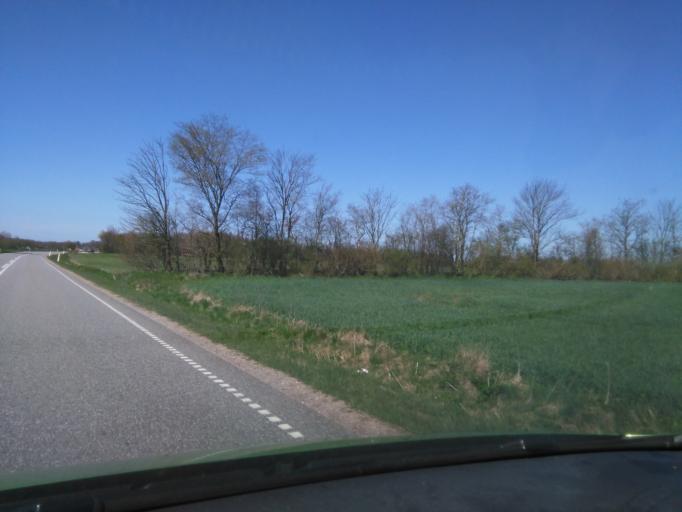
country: DK
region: South Denmark
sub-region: Billund Kommune
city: Grindsted
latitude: 55.7009
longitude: 8.7734
